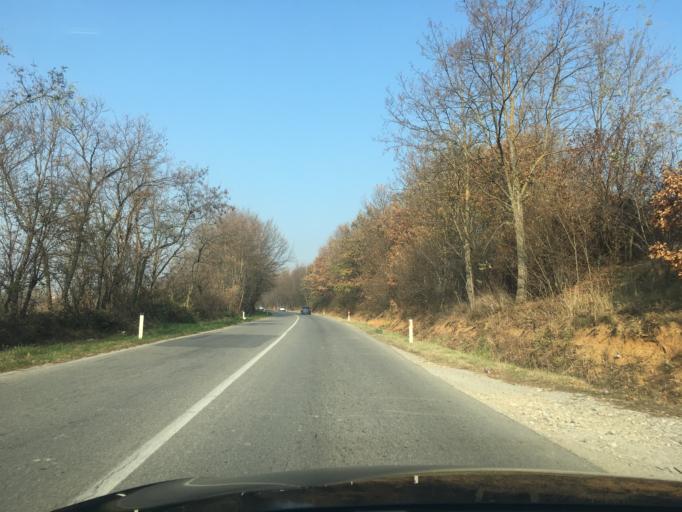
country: XK
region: Pec
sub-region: Komuna e Pejes
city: Dubova (Driloni)
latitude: 42.6457
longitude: 20.4124
